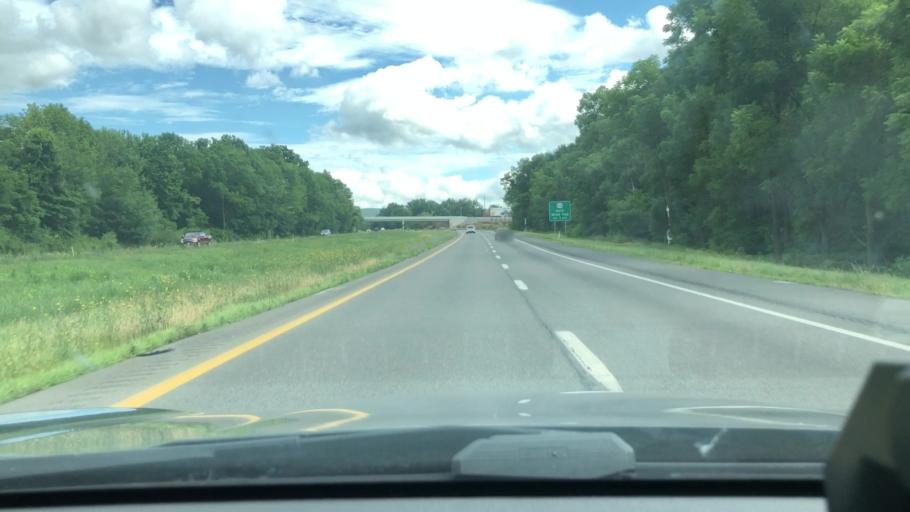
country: US
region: Pennsylvania
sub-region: Northampton County
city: Wind Gap
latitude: 40.8160
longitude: -75.2993
